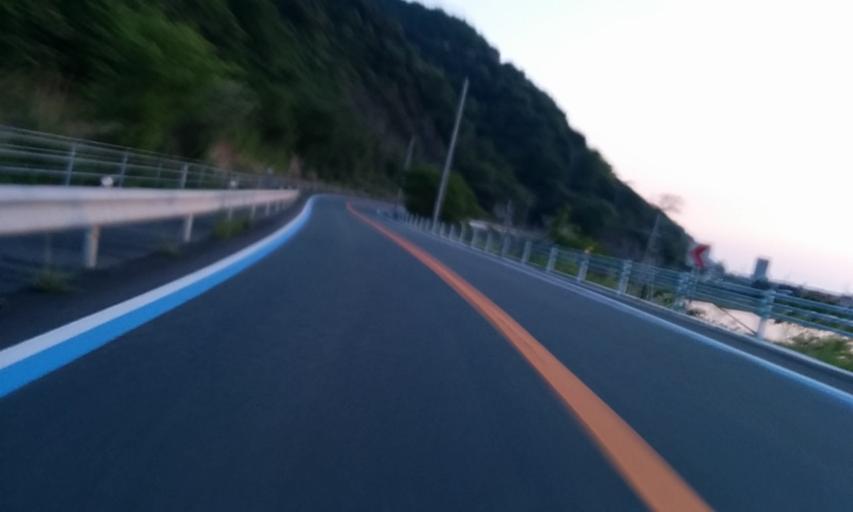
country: JP
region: Ehime
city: Ozu
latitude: 33.6273
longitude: 132.5111
